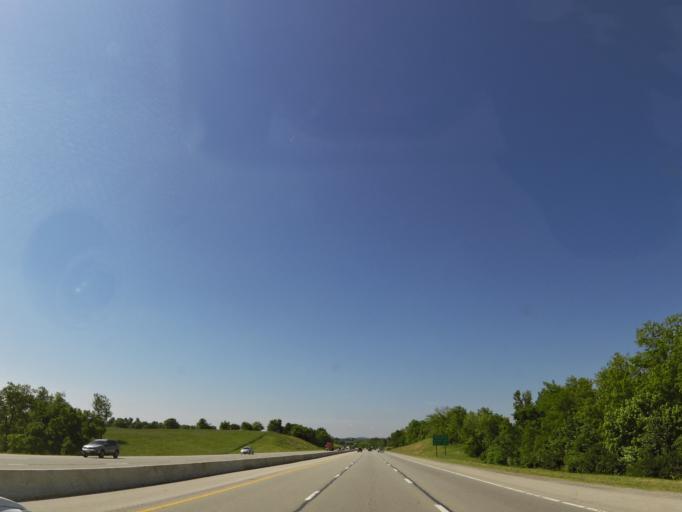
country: US
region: Kentucky
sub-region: Madison County
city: Berea
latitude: 37.6365
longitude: -84.3160
